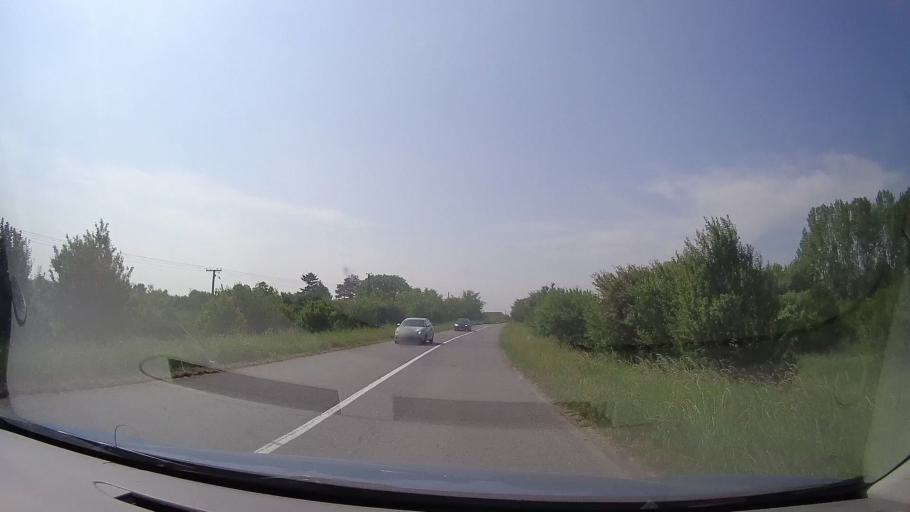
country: RS
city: Jarkovac
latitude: 45.2747
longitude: 20.7644
